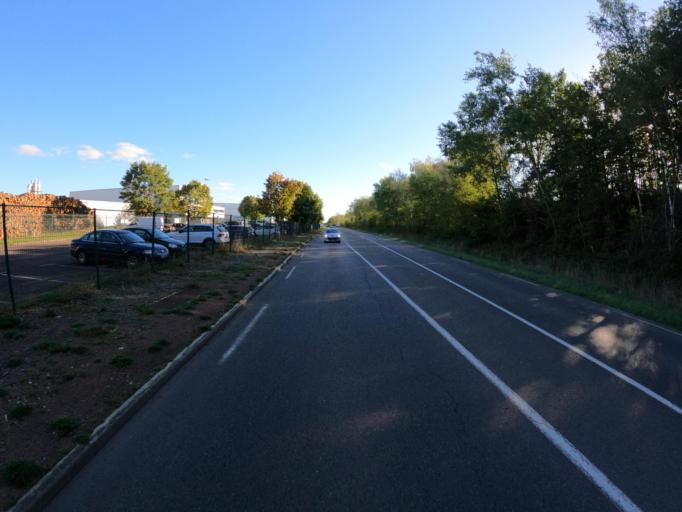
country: FR
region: Bourgogne
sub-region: Departement de Saone-et-Loire
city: Torcy
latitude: 46.7588
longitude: 4.4415
